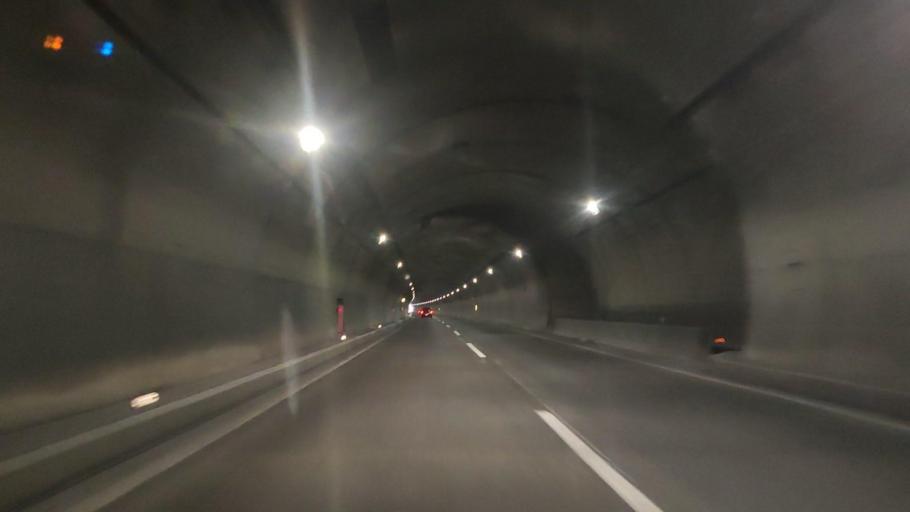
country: JP
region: Oita
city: Beppu
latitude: 33.2741
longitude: 131.3429
